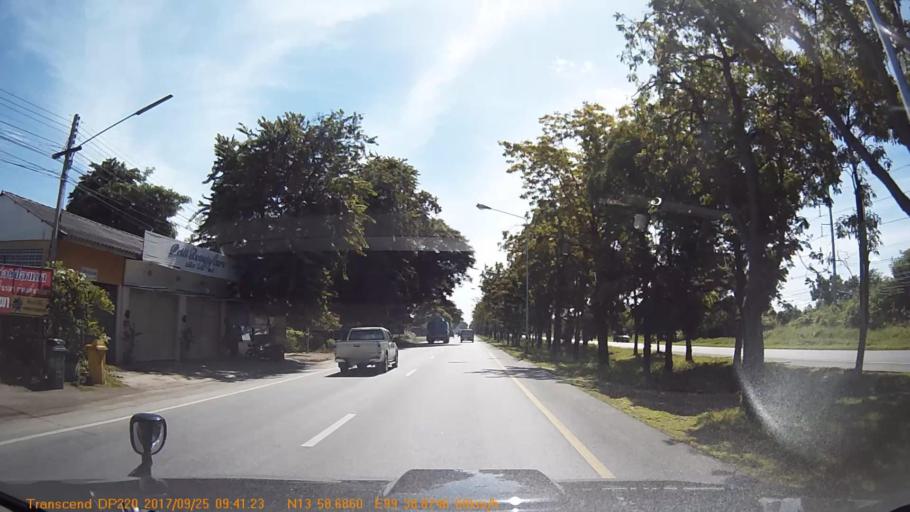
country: TH
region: Kanchanaburi
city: Tha Muang
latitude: 13.9781
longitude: 99.6480
